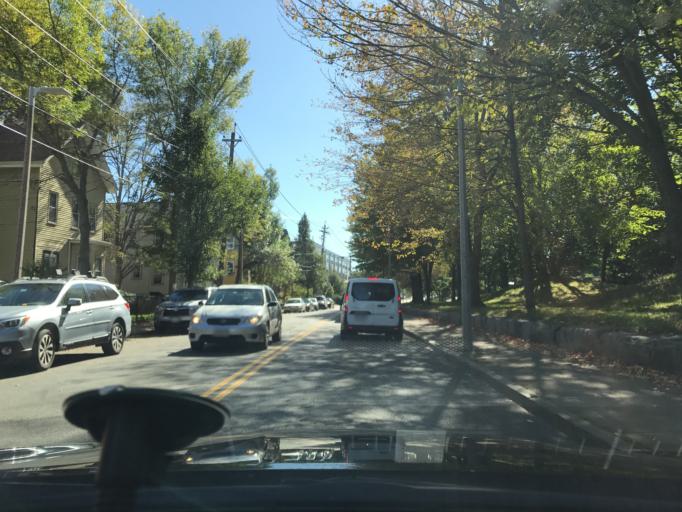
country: US
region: Massachusetts
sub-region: Suffolk County
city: Jamaica Plain
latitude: 42.3136
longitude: -71.1052
